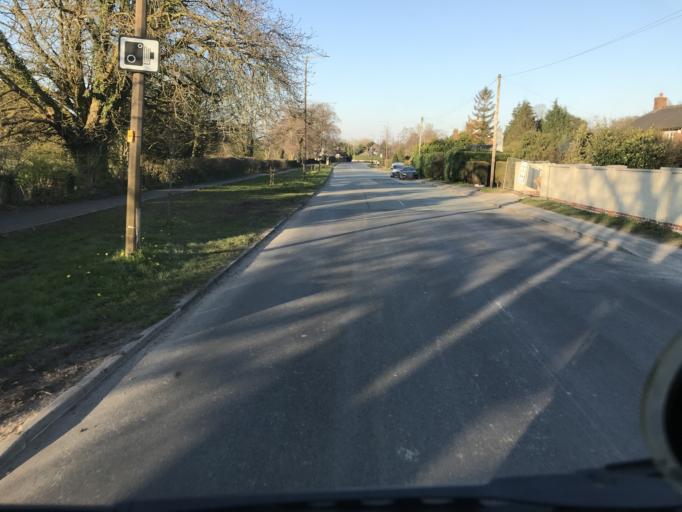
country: GB
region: England
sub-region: Borough of Stockport
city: Bramhall
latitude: 53.3405
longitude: -2.1674
